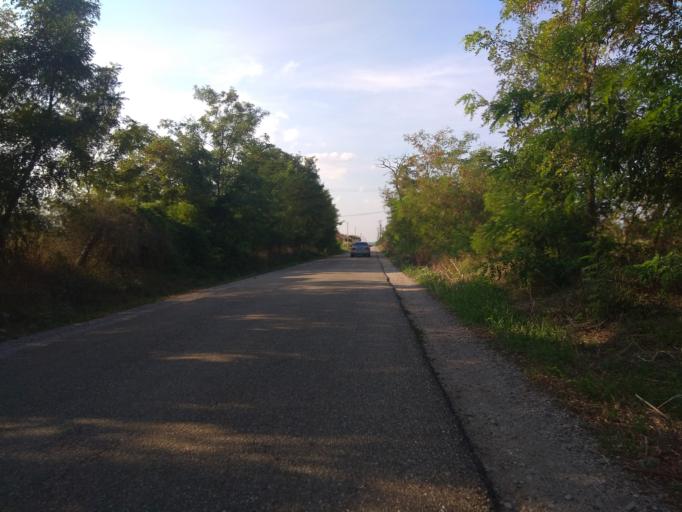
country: HU
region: Borsod-Abauj-Zemplen
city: Harsany
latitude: 47.9138
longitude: 20.7414
